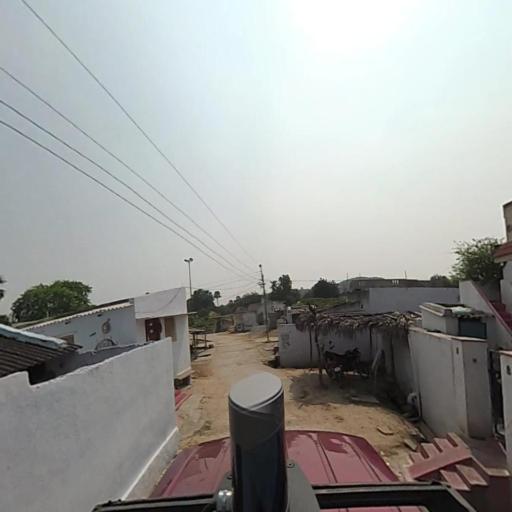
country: IN
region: Telangana
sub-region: Nalgonda
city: Nalgonda
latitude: 17.2101
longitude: 79.1574
